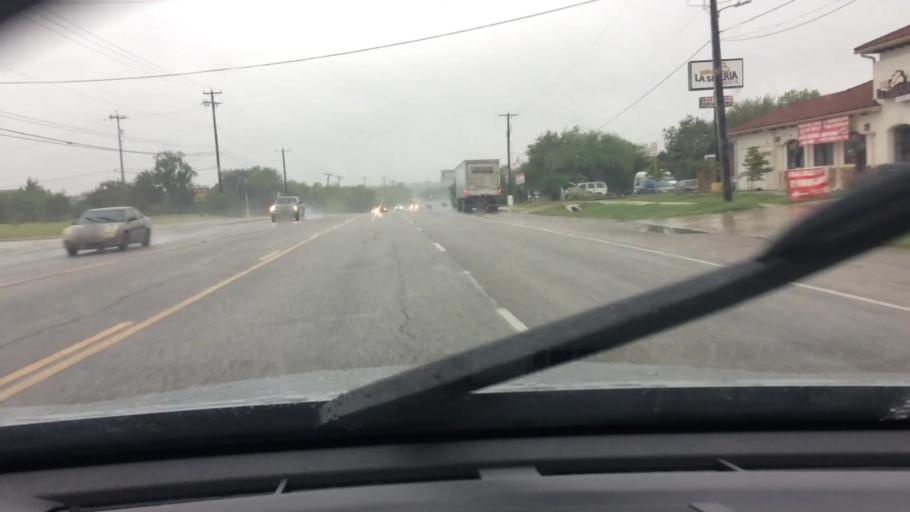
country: US
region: Texas
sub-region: Bexar County
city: Kirby
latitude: 29.4770
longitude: -98.3684
